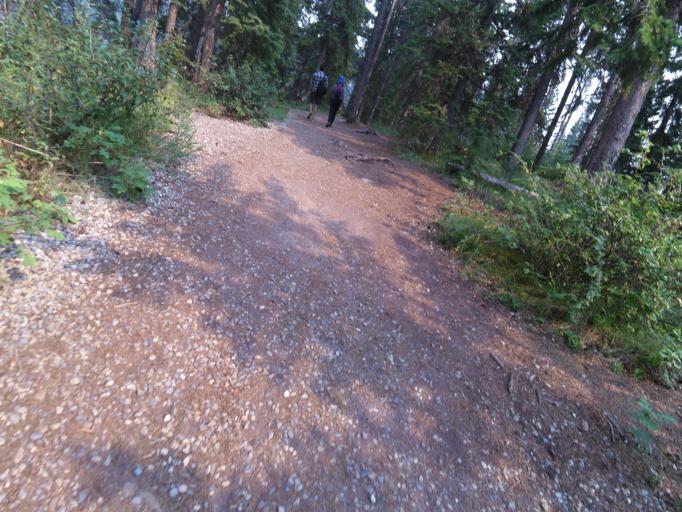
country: CA
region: Alberta
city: Jasper Park Lodge
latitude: 52.9254
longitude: -118.0982
